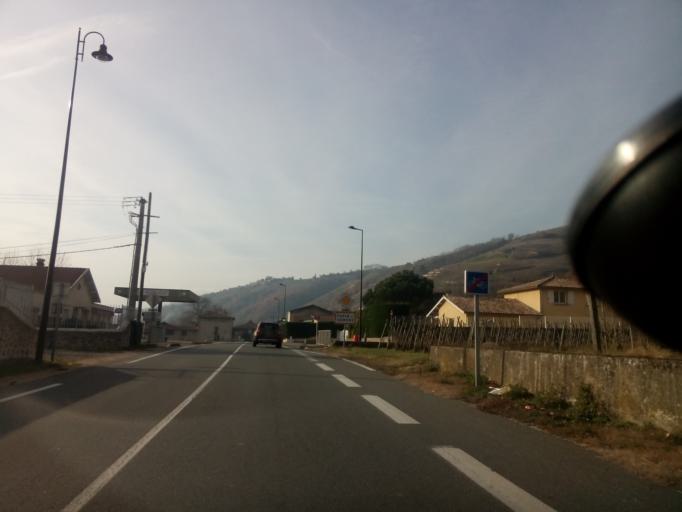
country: FR
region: Rhone-Alpes
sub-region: Departement du Rhone
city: Ampuis
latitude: 45.4851
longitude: 4.7931
